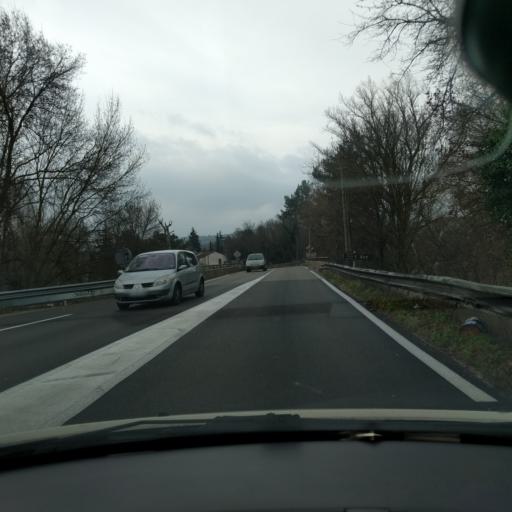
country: FR
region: Provence-Alpes-Cote d'Azur
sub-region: Departement des Bouches-du-Rhone
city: Chateauneuf-le-Rouge
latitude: 43.4833
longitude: 5.5335
